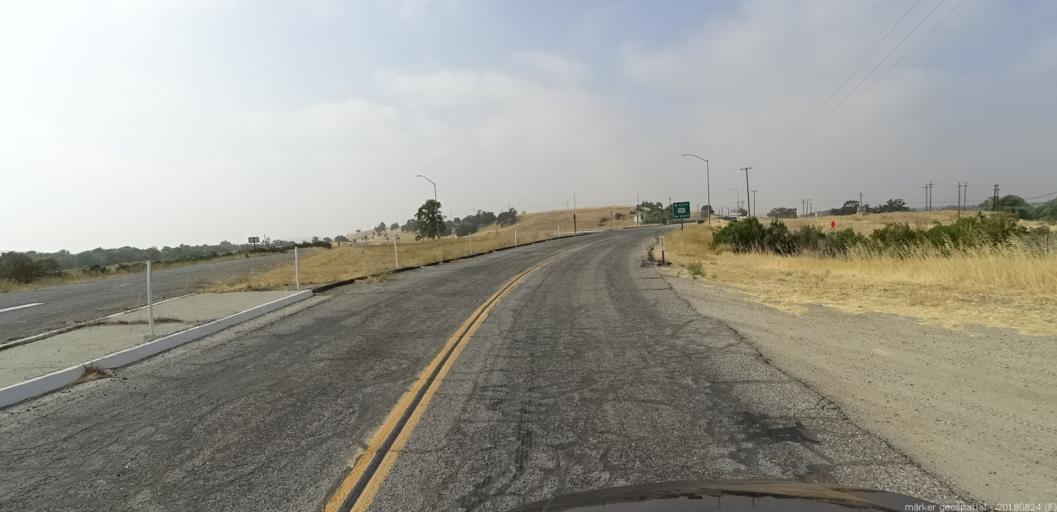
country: US
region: California
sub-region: San Luis Obispo County
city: San Miguel
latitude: 35.8169
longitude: -120.7540
